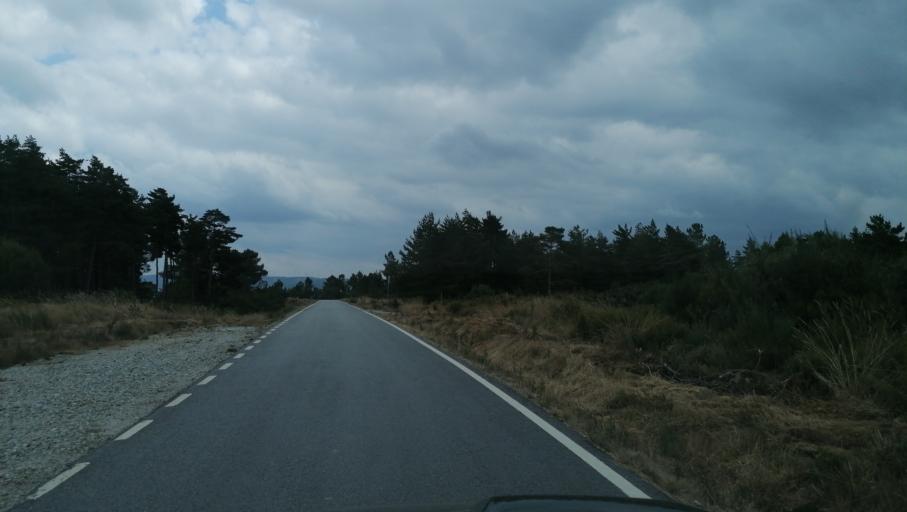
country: PT
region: Vila Real
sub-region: Vila Pouca de Aguiar
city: Vila Pouca de Aguiar
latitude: 41.5449
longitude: -7.6512
